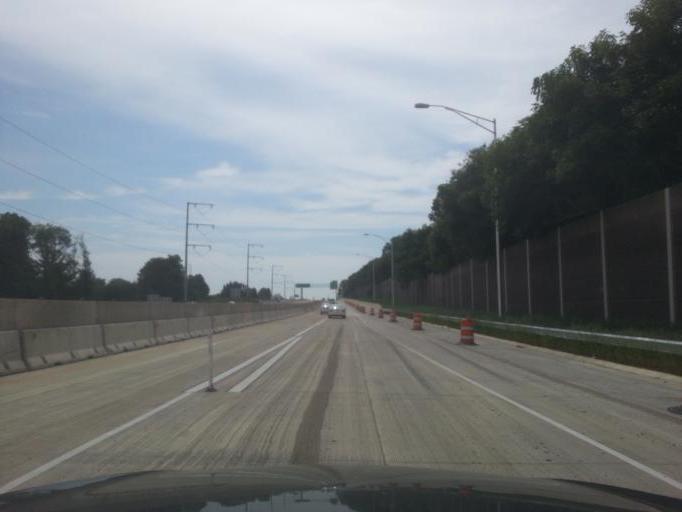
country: US
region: Wisconsin
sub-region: Dane County
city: Shorewood Hills
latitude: 43.0441
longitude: -89.4689
